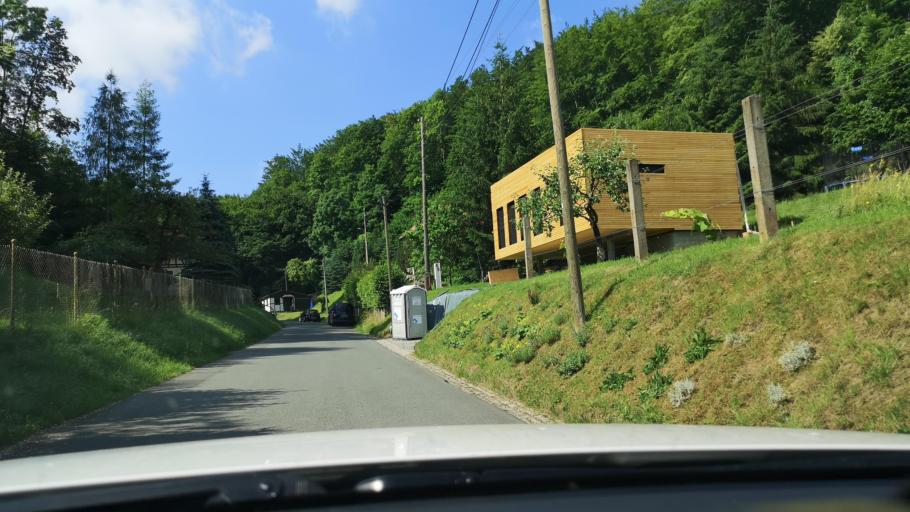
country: DE
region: Thuringia
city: Tautenburg
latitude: 50.9892
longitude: 11.7123
